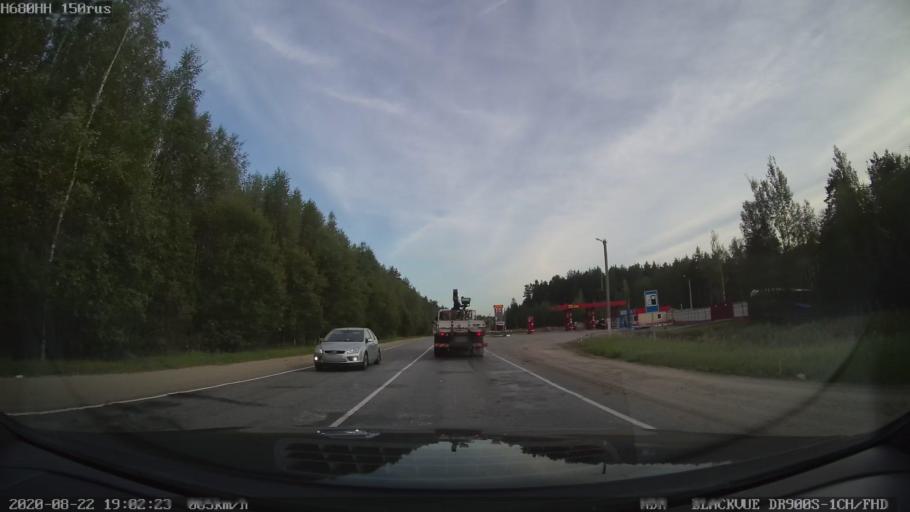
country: RU
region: Tverskaya
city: Sakharovo
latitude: 57.1092
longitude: 36.1199
